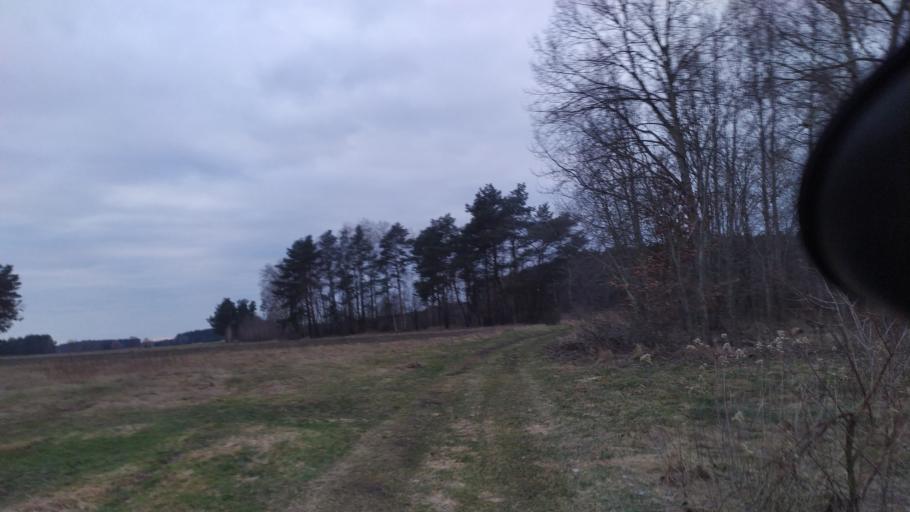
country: PL
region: Lublin Voivodeship
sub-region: Powiat lubartowski
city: Abramow
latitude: 51.4308
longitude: 22.2885
